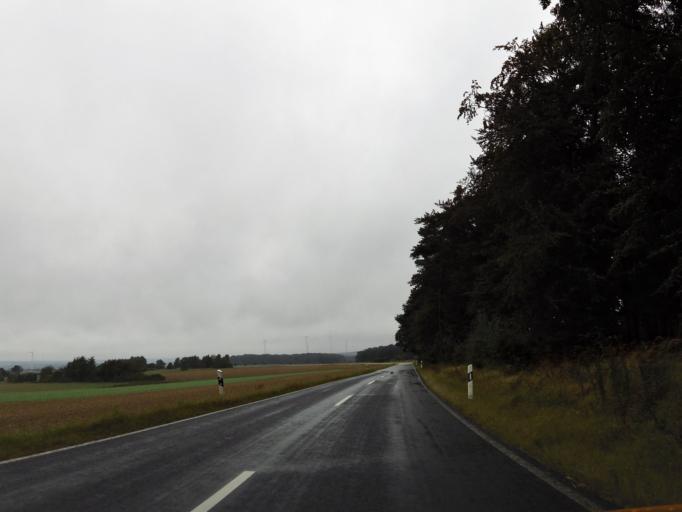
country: DE
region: Rheinland-Pfalz
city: Schnorbach
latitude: 49.9904
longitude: 7.6212
